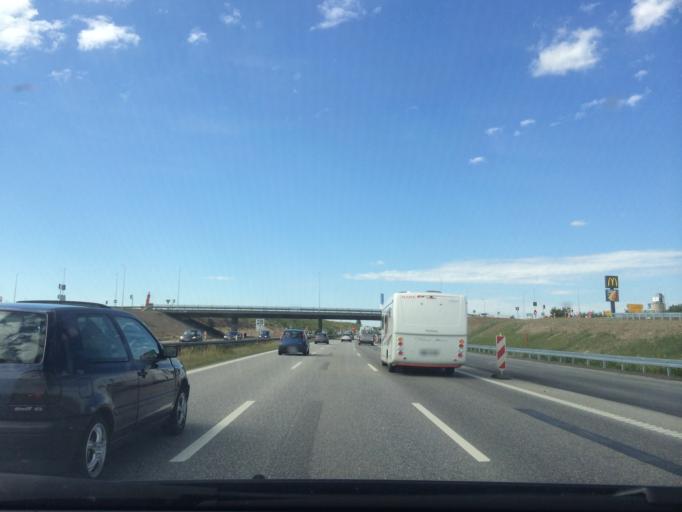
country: DK
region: Zealand
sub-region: Solrod Kommune
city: Solrod Strand
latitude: 55.5468
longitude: 12.2192
